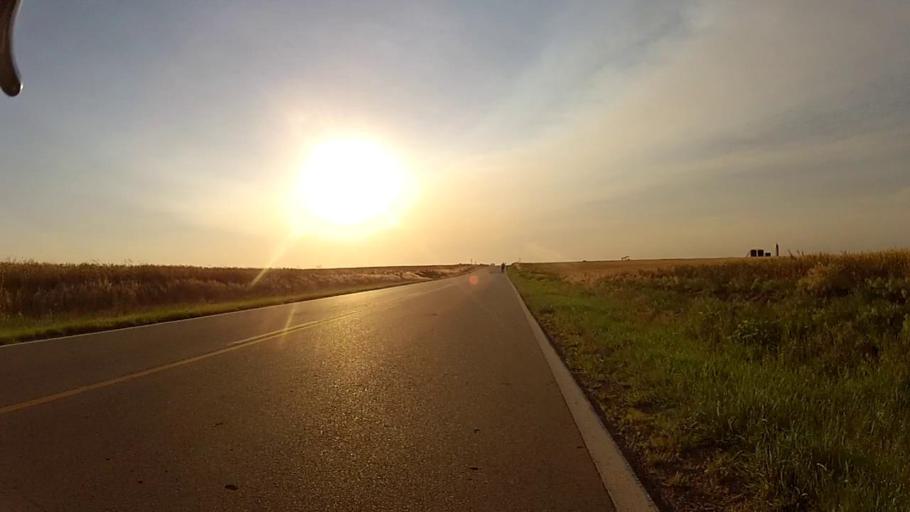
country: US
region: Kansas
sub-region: Harper County
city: Anthony
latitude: 37.1532
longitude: -97.9139
